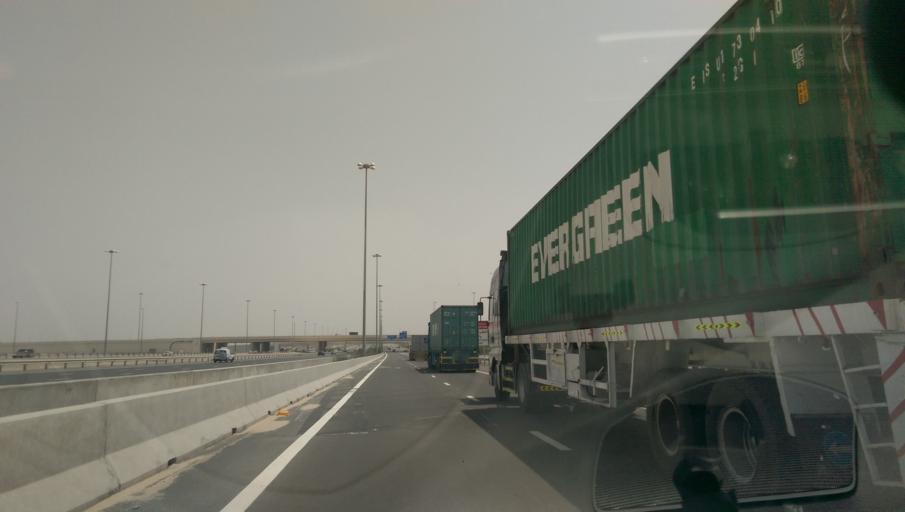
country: AE
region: Abu Dhabi
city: Abu Dhabi
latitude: 24.6908
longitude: 54.7771
